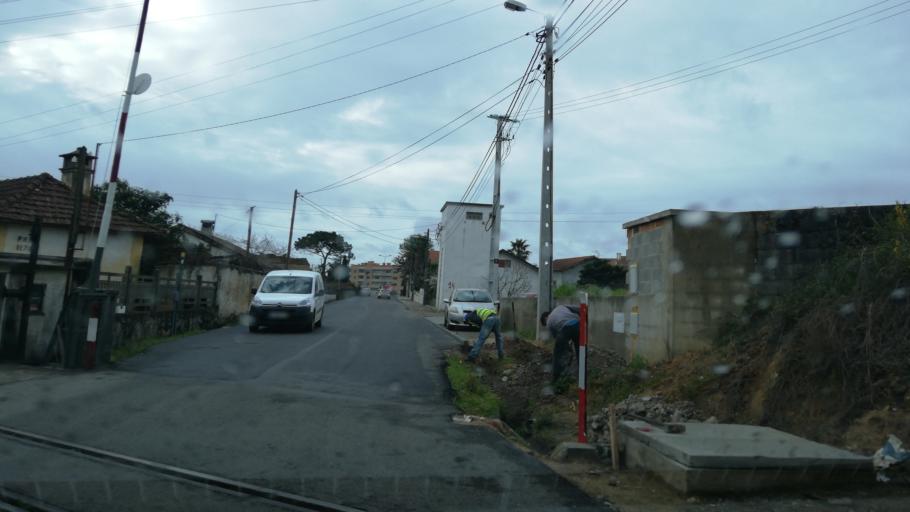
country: PT
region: Aveiro
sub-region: Agueda
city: Agueda
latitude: 40.5927
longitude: -8.4521
